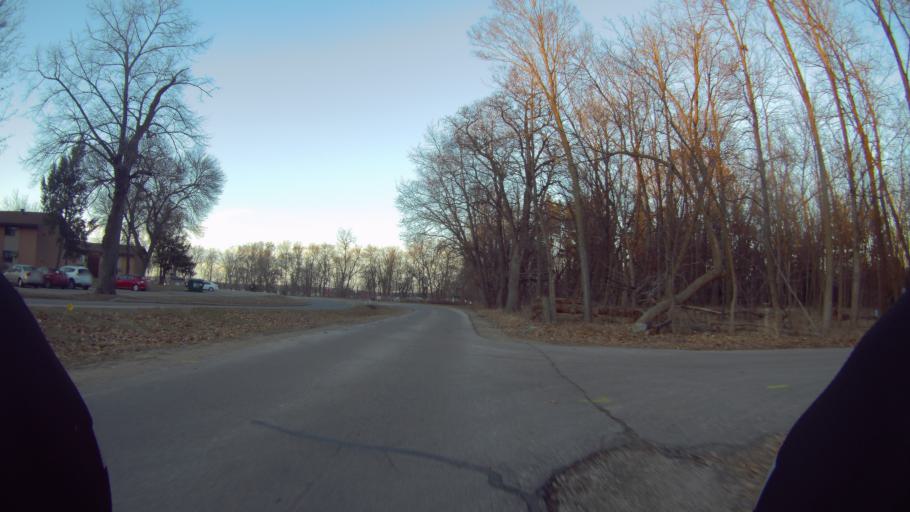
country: US
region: Wisconsin
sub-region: Dane County
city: Shorewood Hills
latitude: 43.0898
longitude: -89.4335
